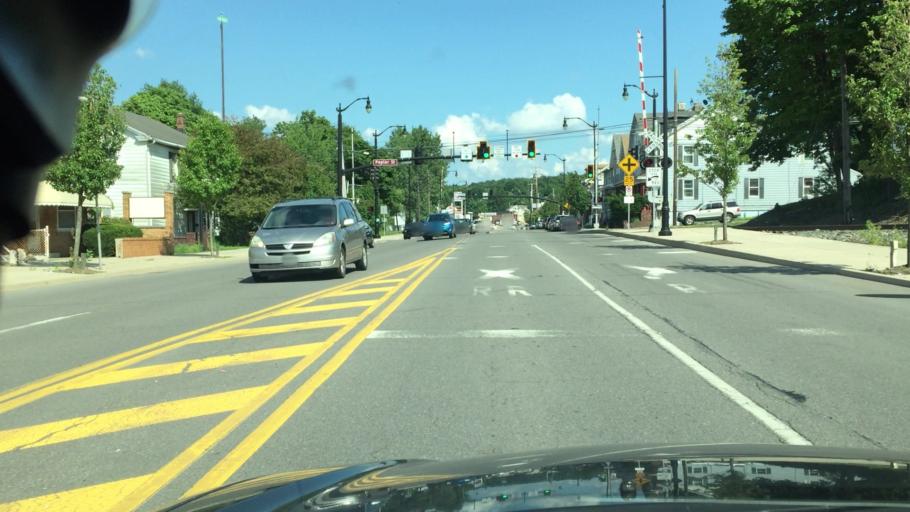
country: US
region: Pennsylvania
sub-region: Luzerne County
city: Hazleton
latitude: 40.9529
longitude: -75.9703
